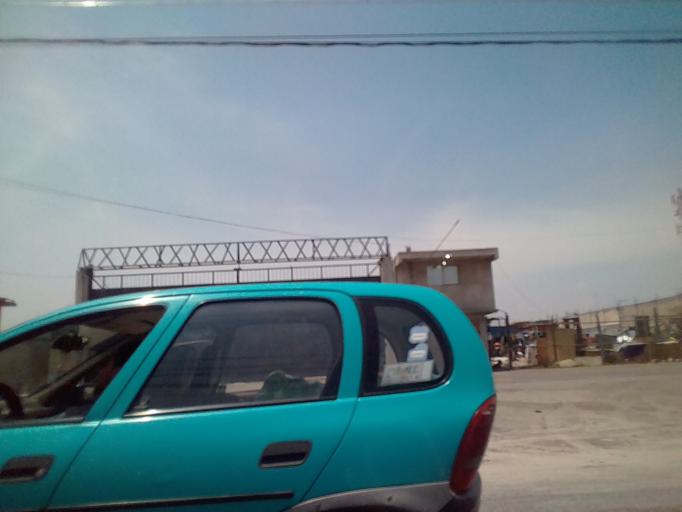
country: MX
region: Mexico
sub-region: Toluca
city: San Nicolas Tolentino
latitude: 19.3656
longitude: -99.5673
